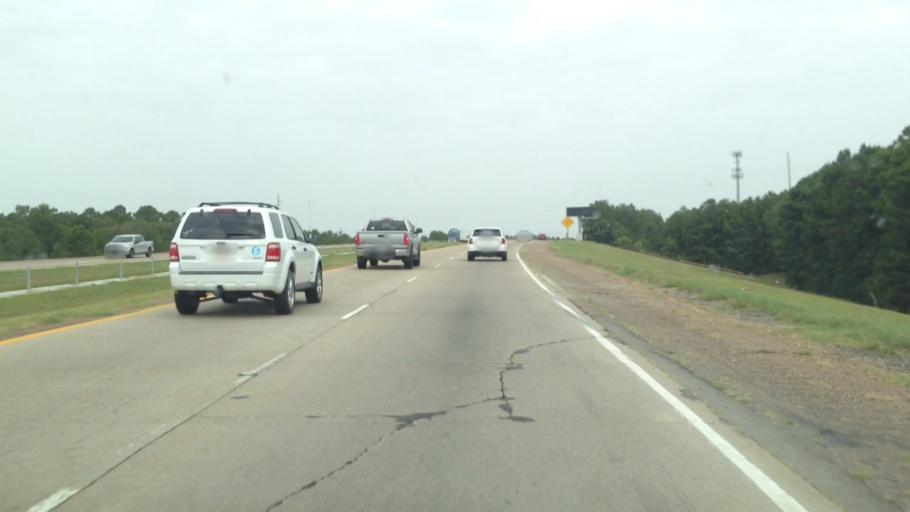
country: US
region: Louisiana
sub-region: Caddo Parish
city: Shreveport
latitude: 32.4183
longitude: -93.8271
